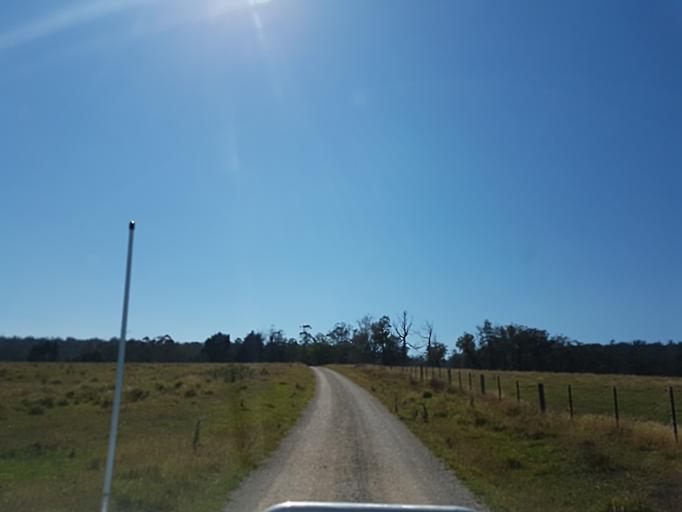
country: AU
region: Victoria
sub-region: East Gippsland
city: Lakes Entrance
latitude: -37.2320
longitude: 148.2723
